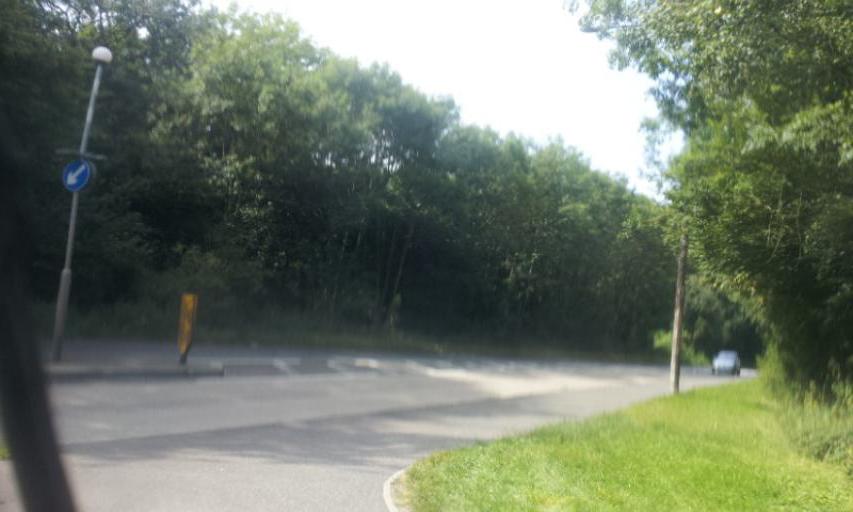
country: GB
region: England
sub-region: Kent
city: Boxley
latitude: 51.3282
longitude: 0.5216
